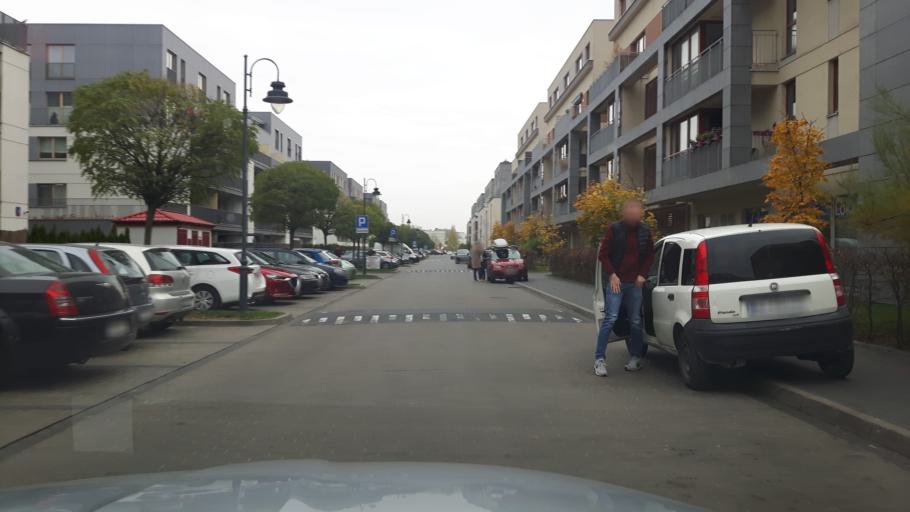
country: PL
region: Masovian Voivodeship
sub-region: Warszawa
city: Ursynow
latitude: 52.1609
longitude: 21.0660
